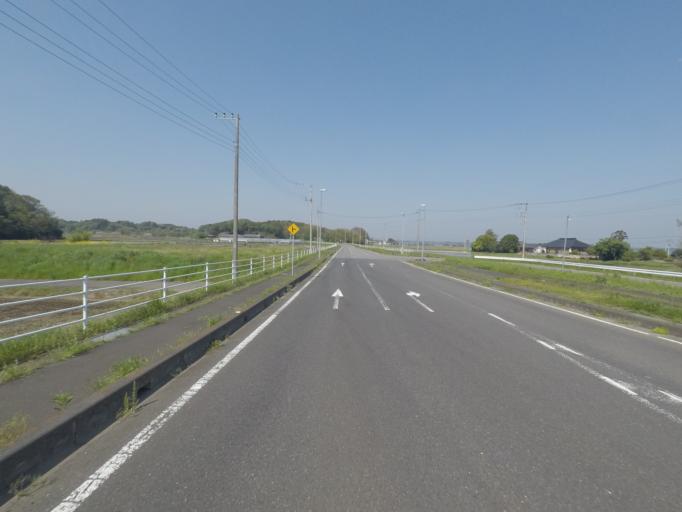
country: JP
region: Ibaraki
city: Inashiki
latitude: 36.0790
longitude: 140.3772
